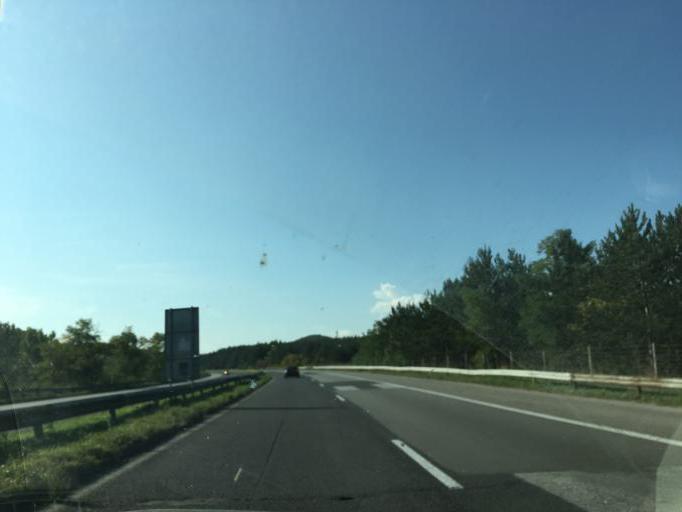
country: BG
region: Sofiya
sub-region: Obshtina Ikhtiman
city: Ikhtiman
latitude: 42.3810
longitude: 23.8771
